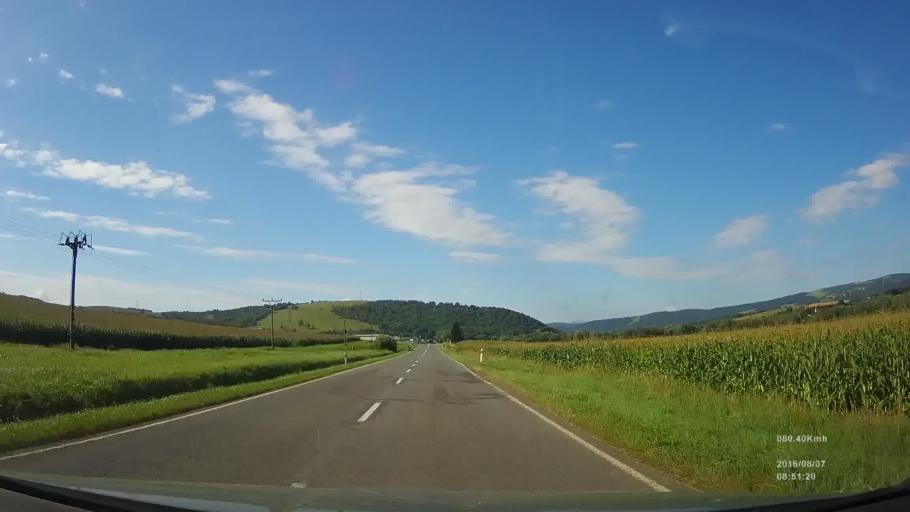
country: SK
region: Presovsky
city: Stropkov
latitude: 49.2390
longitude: 21.6764
